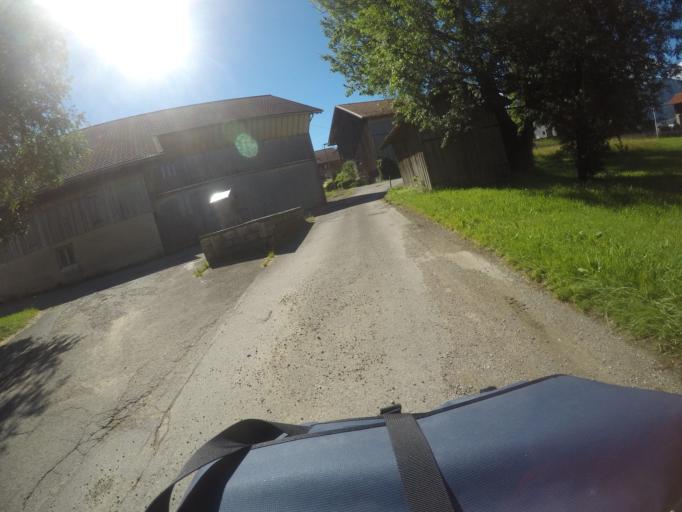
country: DE
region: Bavaria
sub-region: Swabia
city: Pfronten
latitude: 47.6062
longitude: 10.5587
